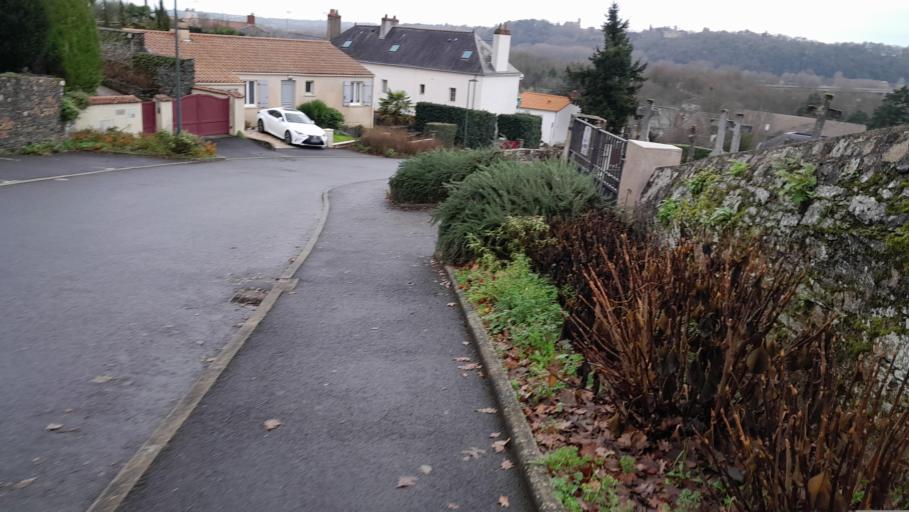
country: FR
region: Pays de la Loire
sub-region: Departement de la Loire-Atlantique
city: Oudon
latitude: 47.3481
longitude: -1.2846
